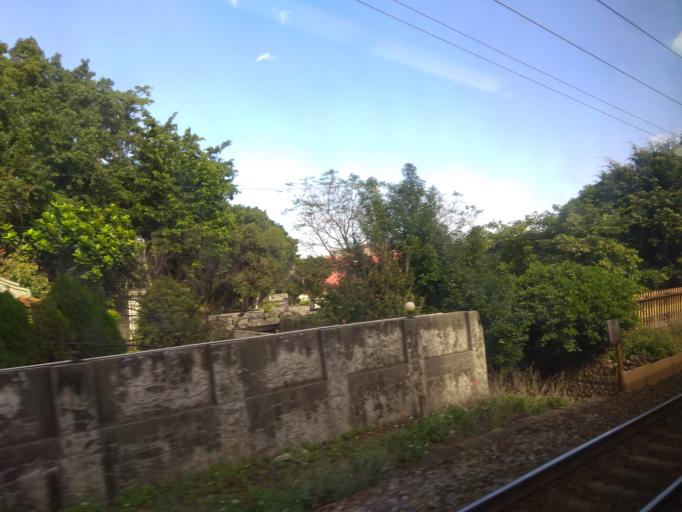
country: TW
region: Taiwan
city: Taoyuan City
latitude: 24.9588
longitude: 121.2379
